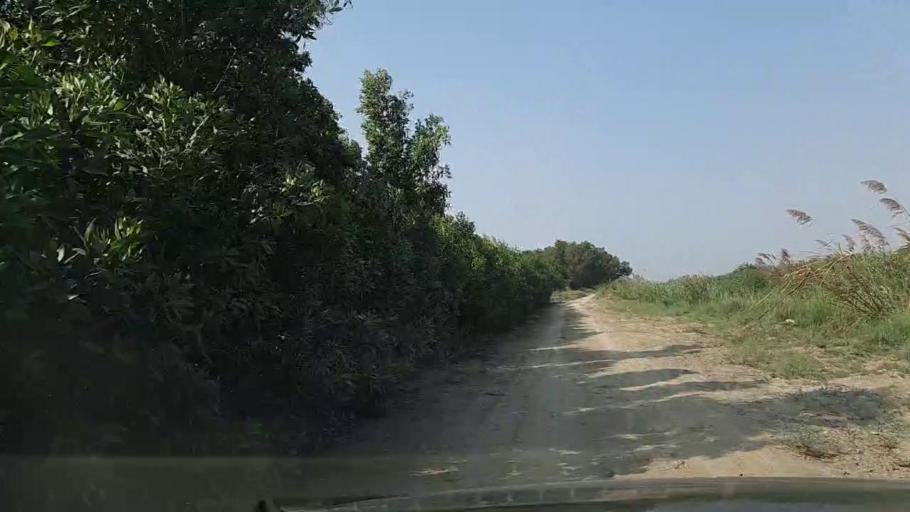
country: PK
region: Sindh
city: Gharo
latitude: 24.7219
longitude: 67.6756
